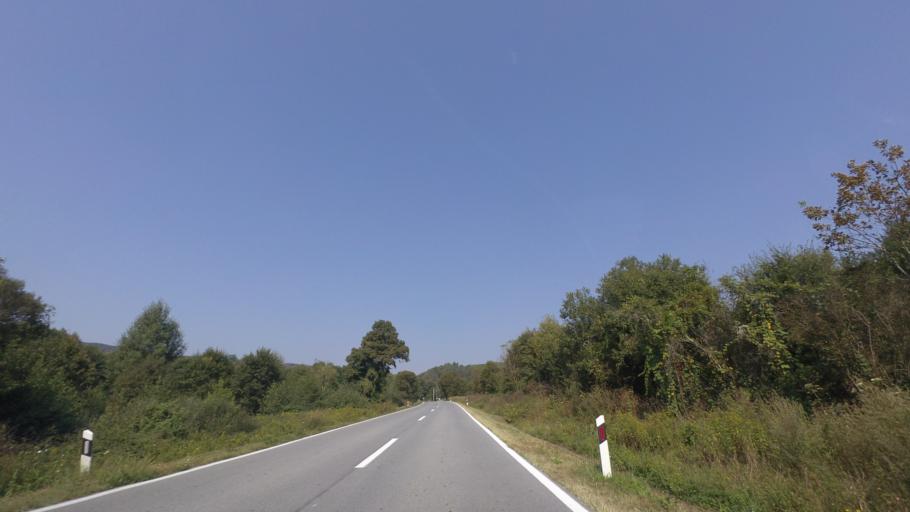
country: HR
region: Pozesko-Slavonska
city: Velika
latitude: 45.4409
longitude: 17.4849
